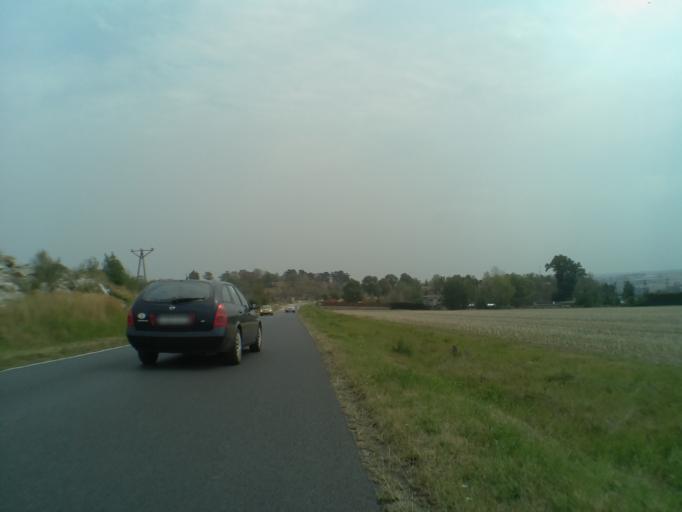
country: PL
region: Lower Silesian Voivodeship
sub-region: Powiat swidnicki
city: Strzegom
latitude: 50.9656
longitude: 16.3334
